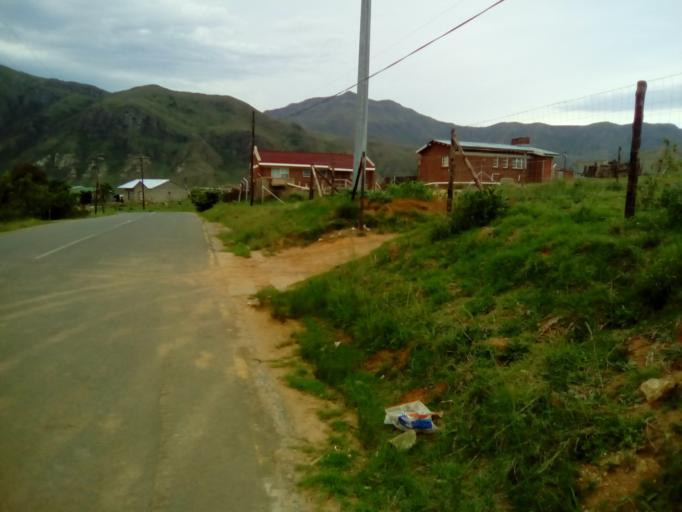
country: LS
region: Qacha's Nek
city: Qacha's Nek
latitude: -30.1082
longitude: 28.6817
